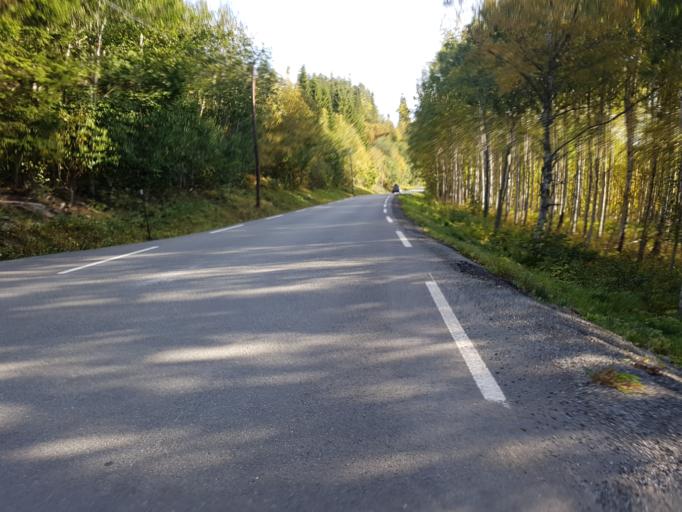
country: NO
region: Sor-Trondelag
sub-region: Malvik
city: Malvik
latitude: 63.3674
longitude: 10.6207
